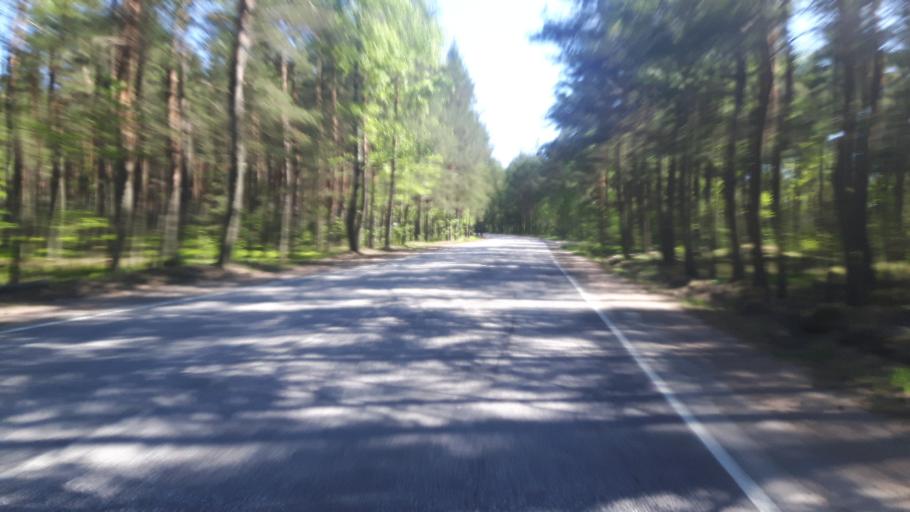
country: RU
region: Leningrad
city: Glebychevo
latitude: 60.2908
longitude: 28.8700
